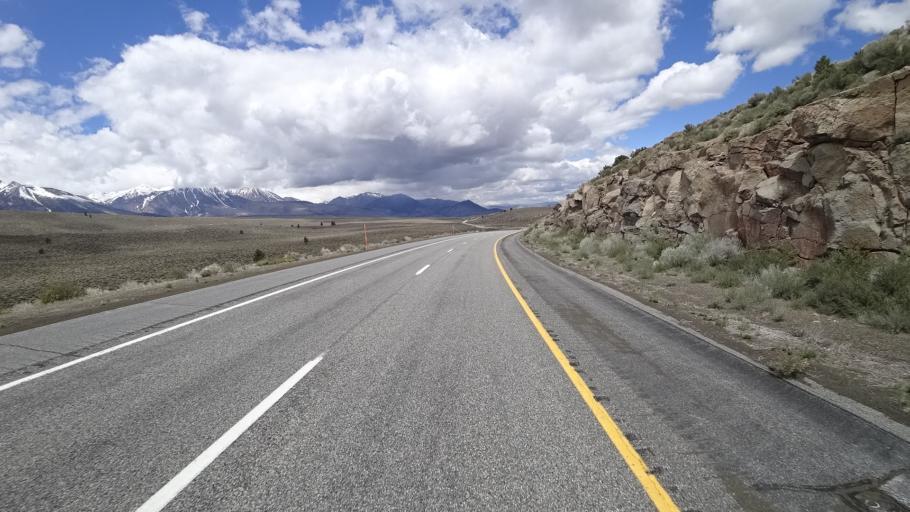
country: US
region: California
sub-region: Mono County
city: Mammoth Lakes
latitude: 37.8321
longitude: -119.0725
